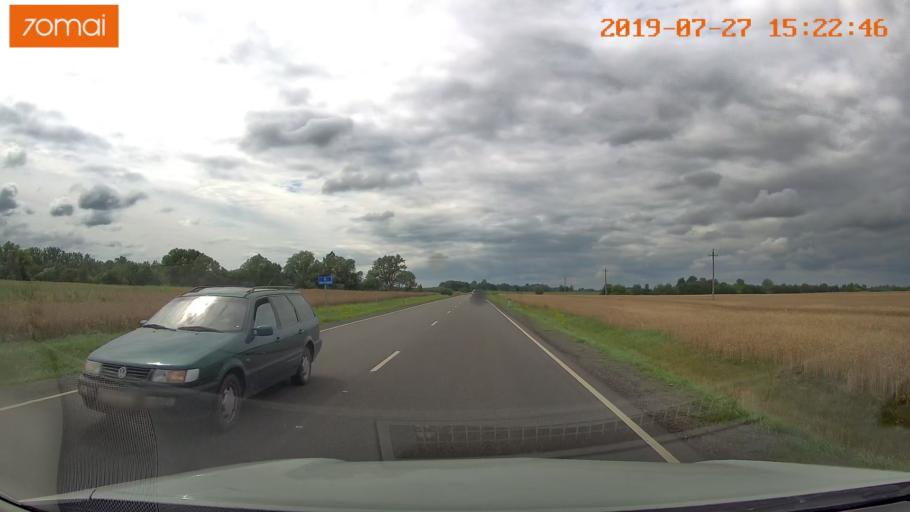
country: RU
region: Kaliningrad
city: Nesterov
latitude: 54.6342
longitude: 22.6504
